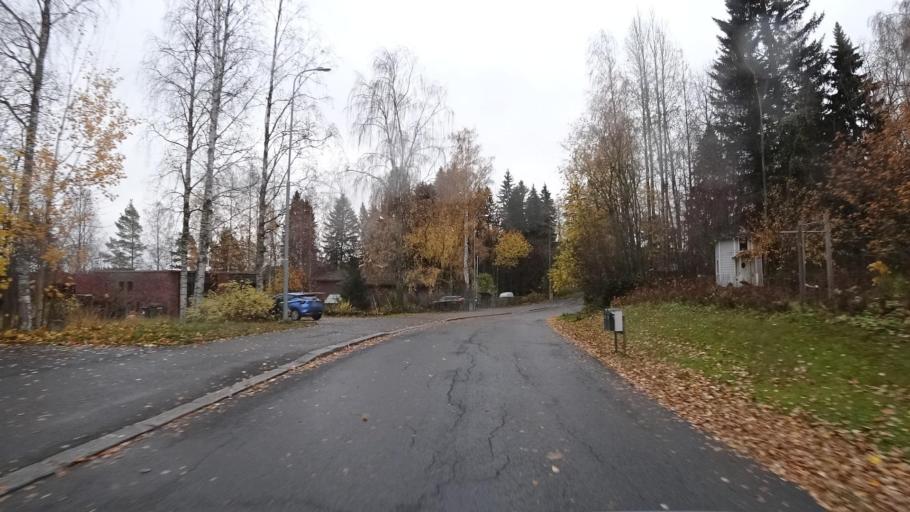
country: FI
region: Northern Savo
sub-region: Kuopio
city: Kuopio
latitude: 62.9275
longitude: 27.6956
